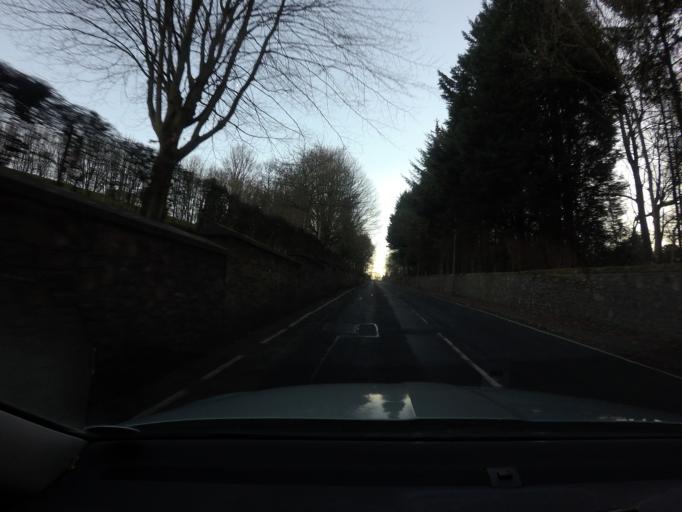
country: GB
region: Scotland
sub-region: Fife
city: Newport-On-Tay
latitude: 56.4368
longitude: -2.9374
